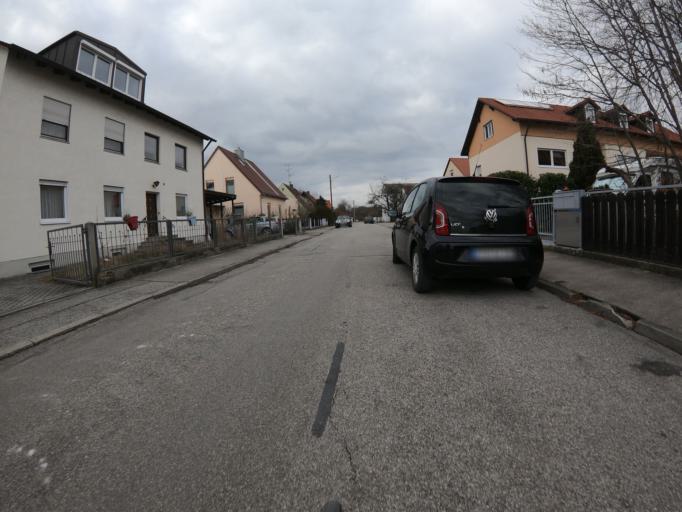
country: DE
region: Bavaria
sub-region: Upper Bavaria
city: Fuerstenfeldbruck
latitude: 48.1864
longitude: 11.2621
